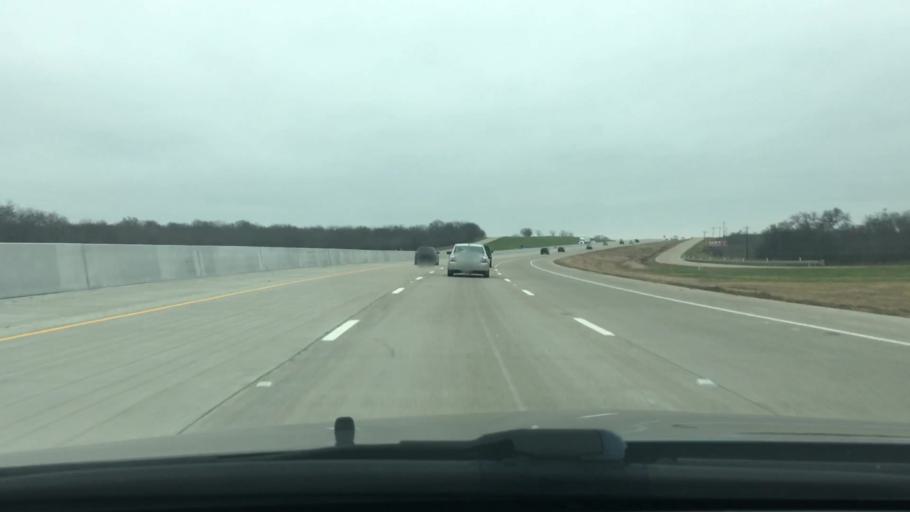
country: US
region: Texas
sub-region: Freestone County
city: Wortham
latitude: 31.8899
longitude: -96.3558
